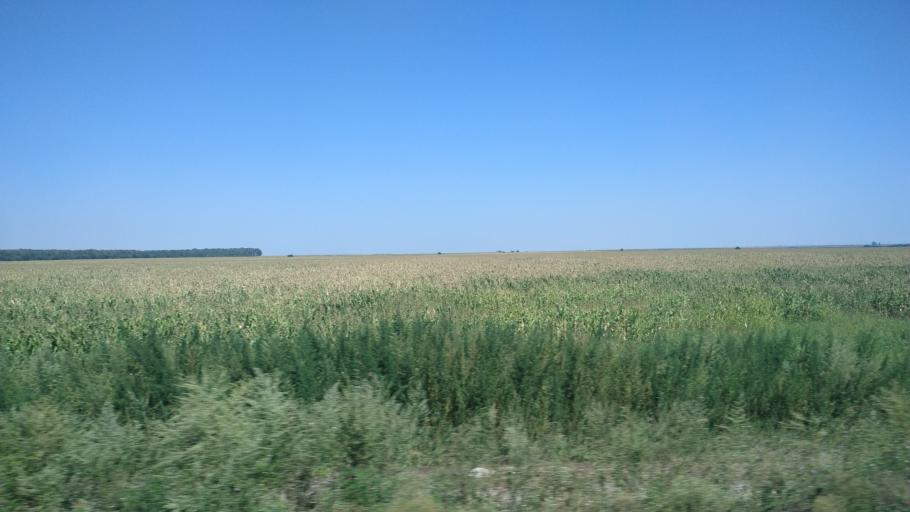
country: RO
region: Calarasi
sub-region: Comuna Perisoru
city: Perisoru
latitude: 44.4220
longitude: 27.6165
